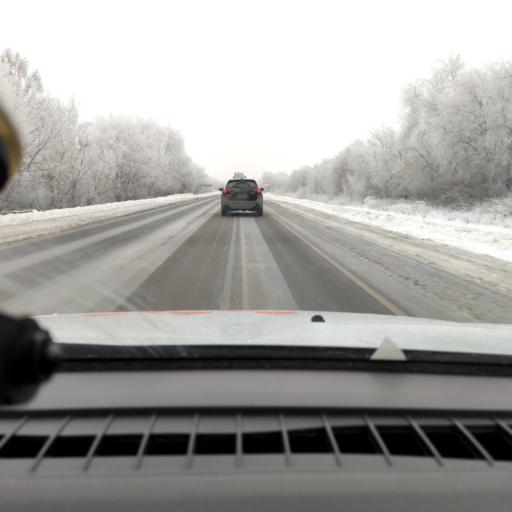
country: RU
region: Samara
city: Samara
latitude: 53.0817
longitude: 50.1626
